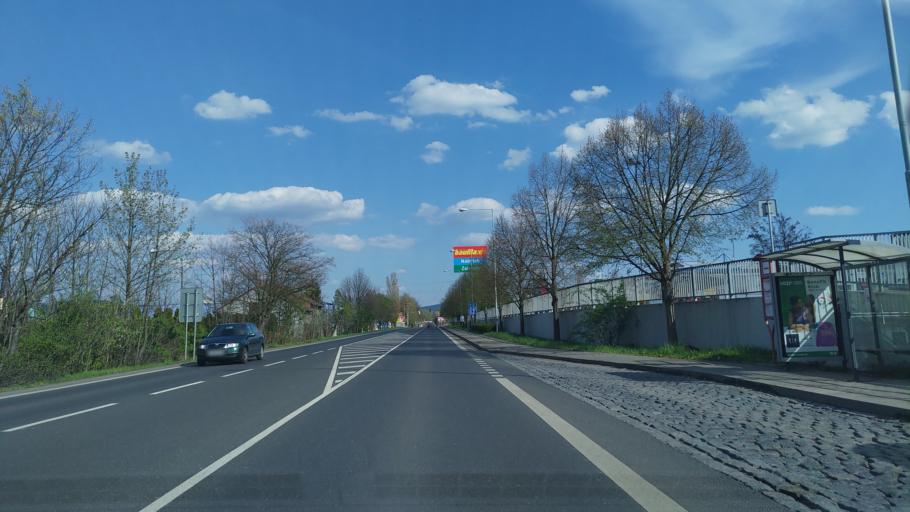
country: CZ
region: Ustecky
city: Chabarovice
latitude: 50.6897
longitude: 13.9843
